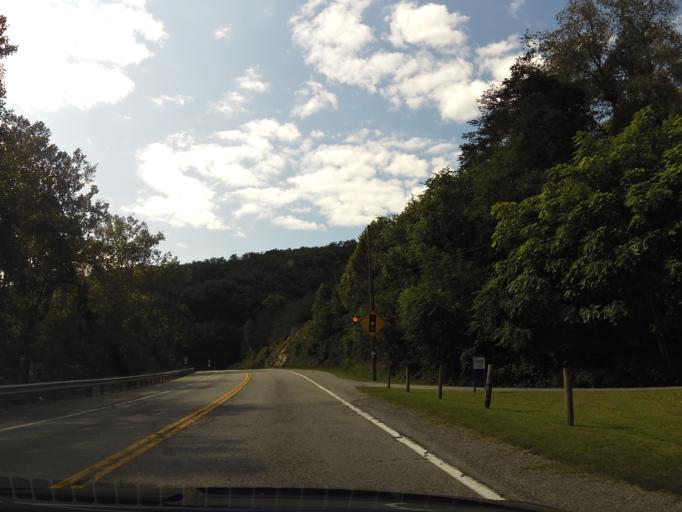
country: US
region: Kentucky
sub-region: Bell County
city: Pineville
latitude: 36.7473
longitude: -83.6889
